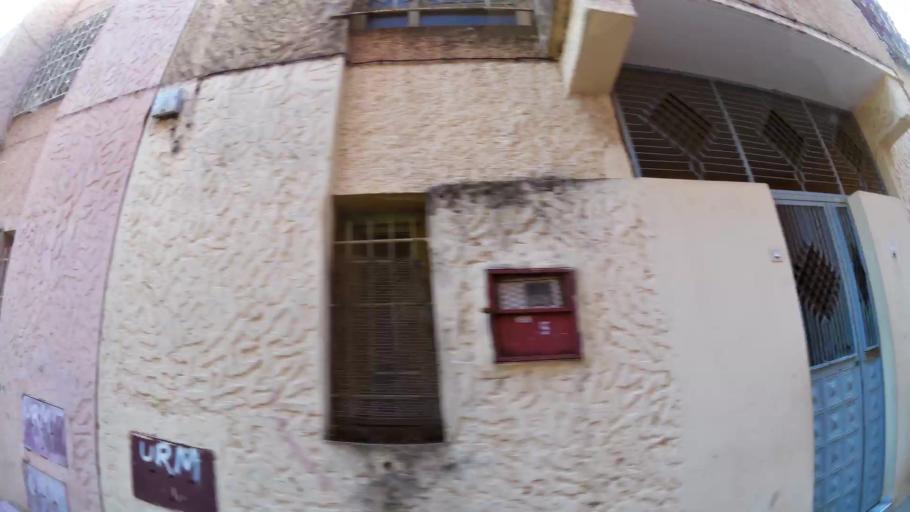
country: MA
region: Meknes-Tafilalet
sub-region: Meknes
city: Meknes
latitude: 33.8976
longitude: -5.5045
